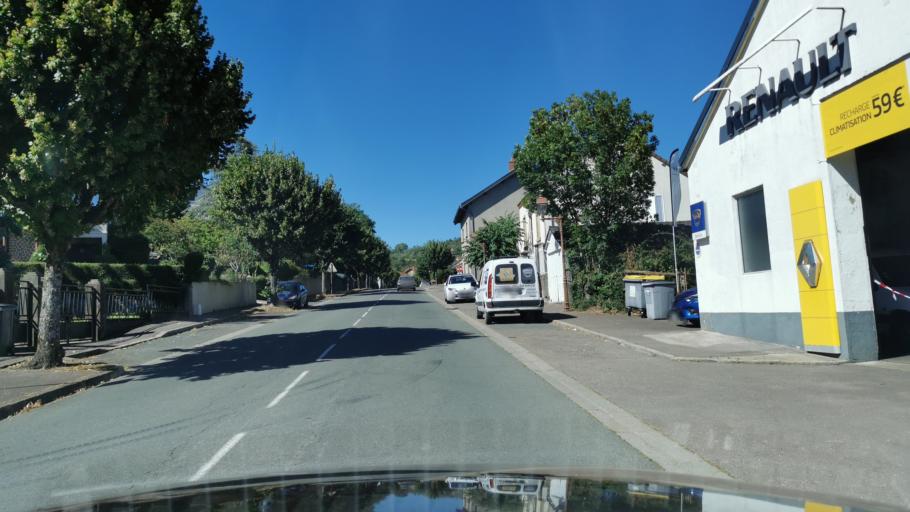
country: FR
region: Bourgogne
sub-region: Departement de Saone-et-Loire
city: Montcenis
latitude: 46.7941
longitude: 4.3891
